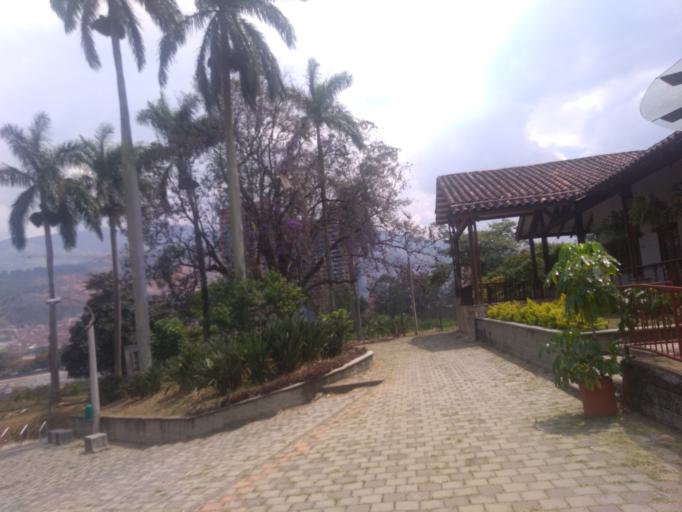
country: CO
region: Antioquia
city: Bello
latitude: 6.3269
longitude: -75.5622
